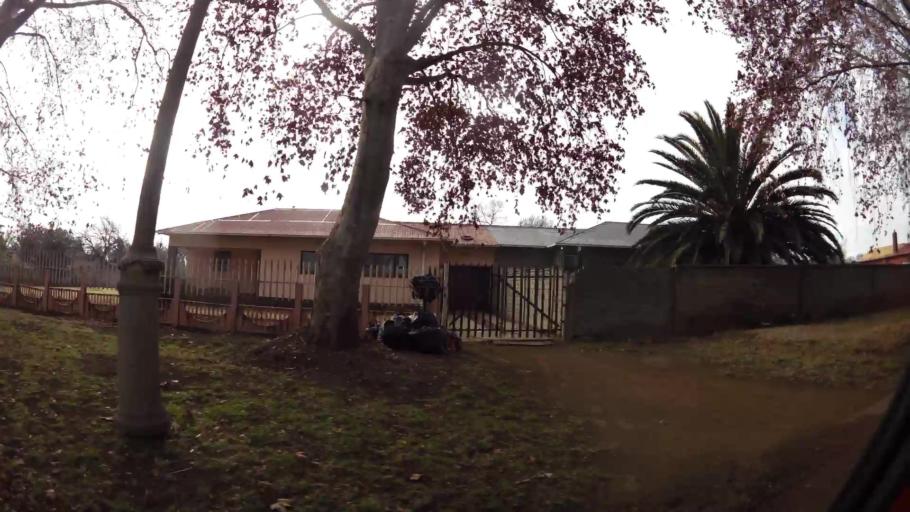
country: ZA
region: Gauteng
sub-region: Sedibeng District Municipality
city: Vanderbijlpark
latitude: -26.6843
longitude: 27.8164
